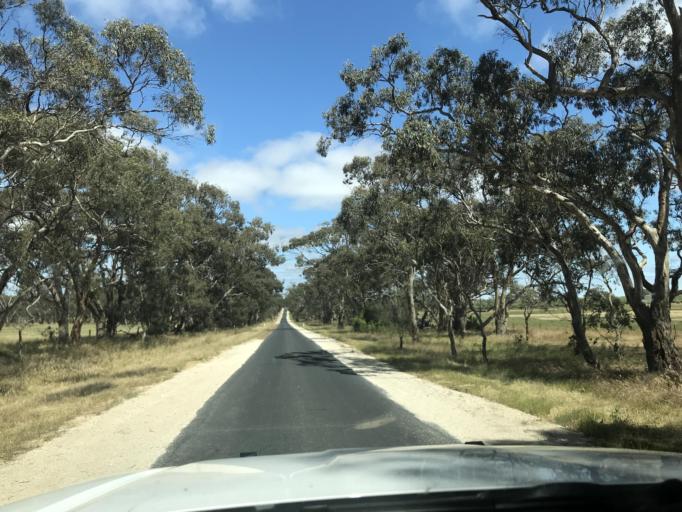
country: AU
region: South Australia
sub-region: Tatiara
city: Bordertown
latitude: -36.3063
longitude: 141.0708
